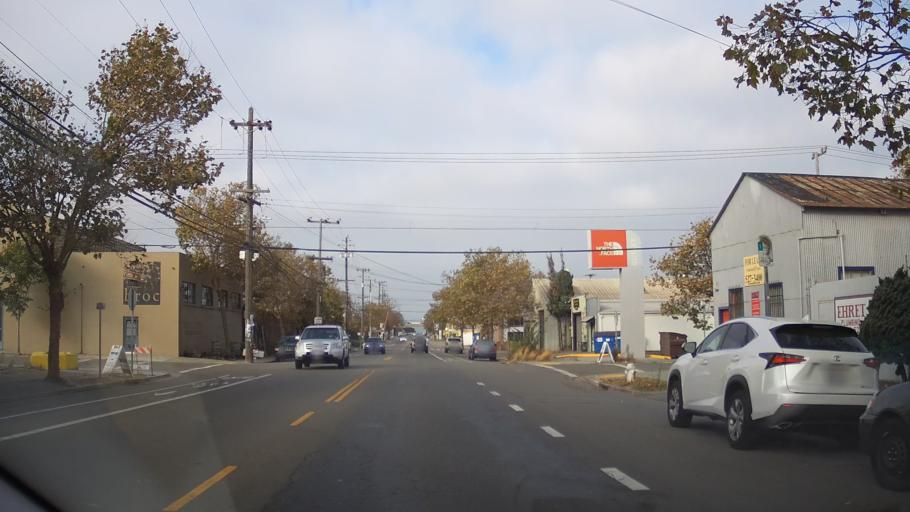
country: US
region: California
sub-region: Alameda County
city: Albany
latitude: 37.8792
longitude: -122.3021
